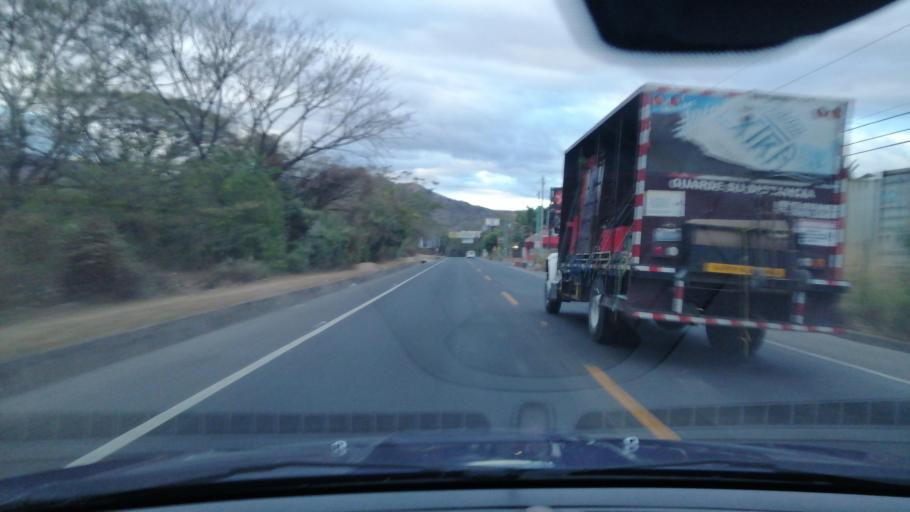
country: SV
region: Santa Ana
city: Santa Ana
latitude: 14.0033
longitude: -89.5418
